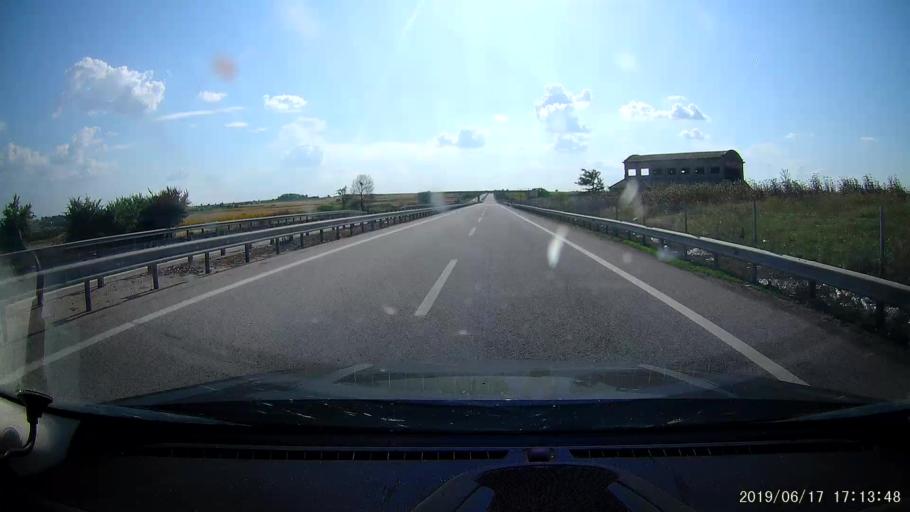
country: TR
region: Edirne
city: Edirne
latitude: 41.7004
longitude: 26.5325
